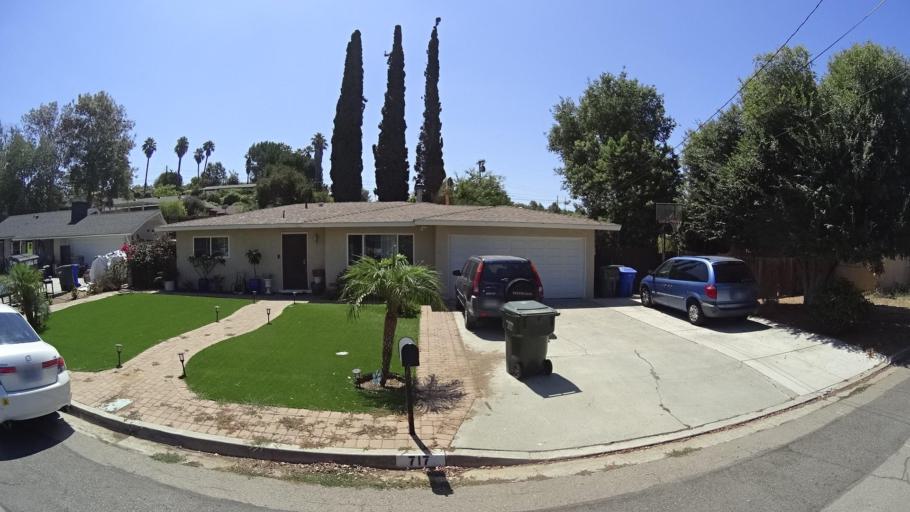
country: US
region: California
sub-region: San Diego County
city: Fallbrook
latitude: 33.3780
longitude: -117.2440
